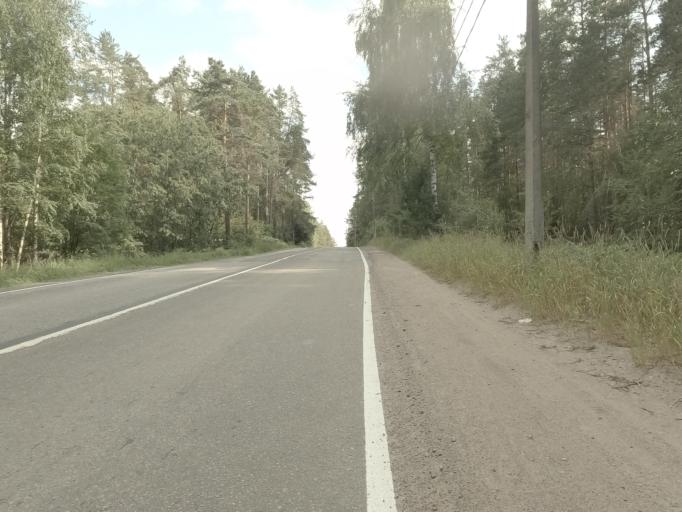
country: RU
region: Leningrad
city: Kamennogorsk
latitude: 60.9374
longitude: 29.1570
